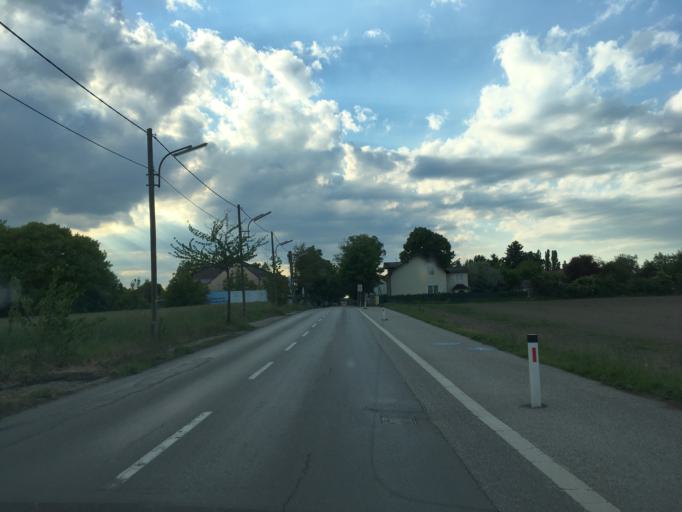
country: AT
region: Lower Austria
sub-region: Politischer Bezirk Wien-Umgebung
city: Gerasdorf bei Wien
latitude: 48.2821
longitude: 16.4886
